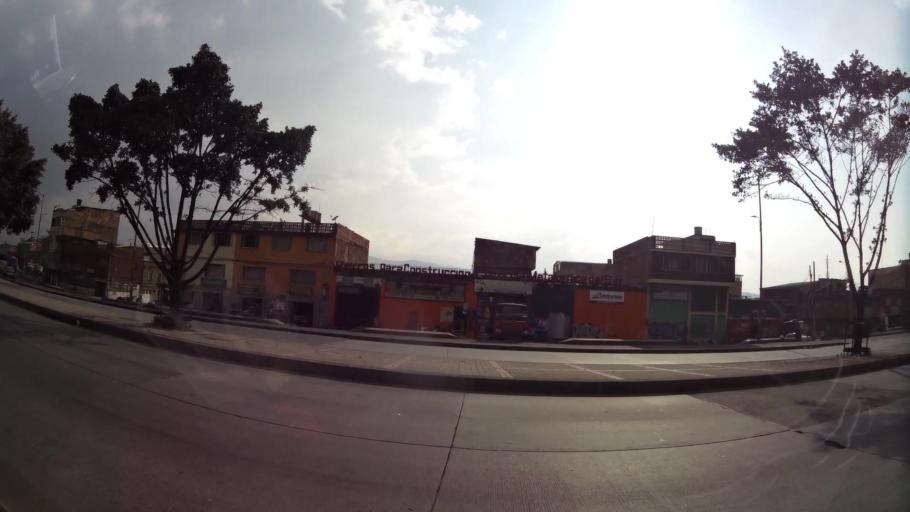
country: CO
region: Bogota D.C.
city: Bogota
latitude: 4.5639
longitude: -74.1250
